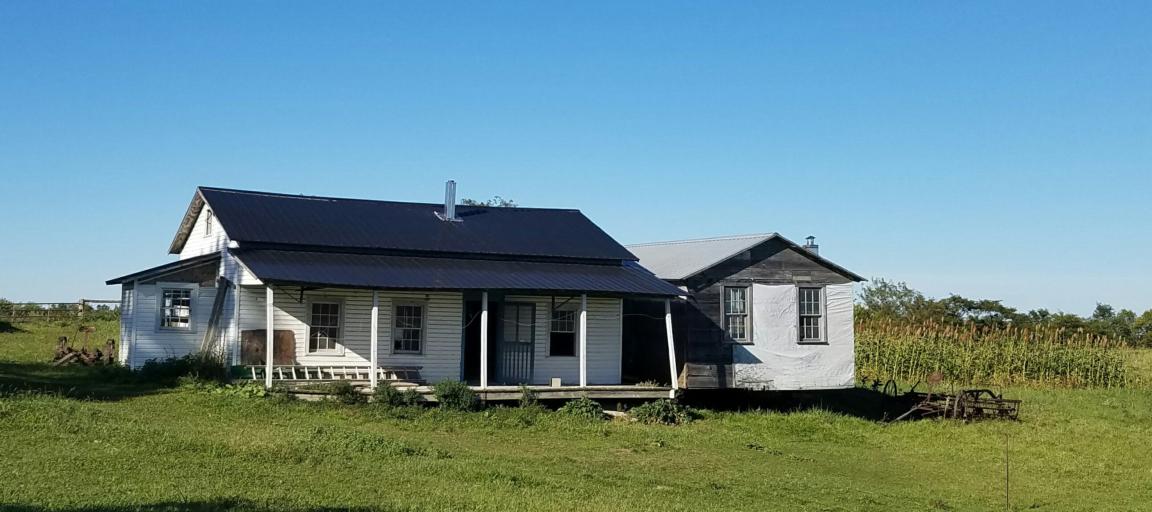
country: US
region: Iowa
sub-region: Decatur County
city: Lamoni
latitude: 40.6382
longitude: -93.8794
